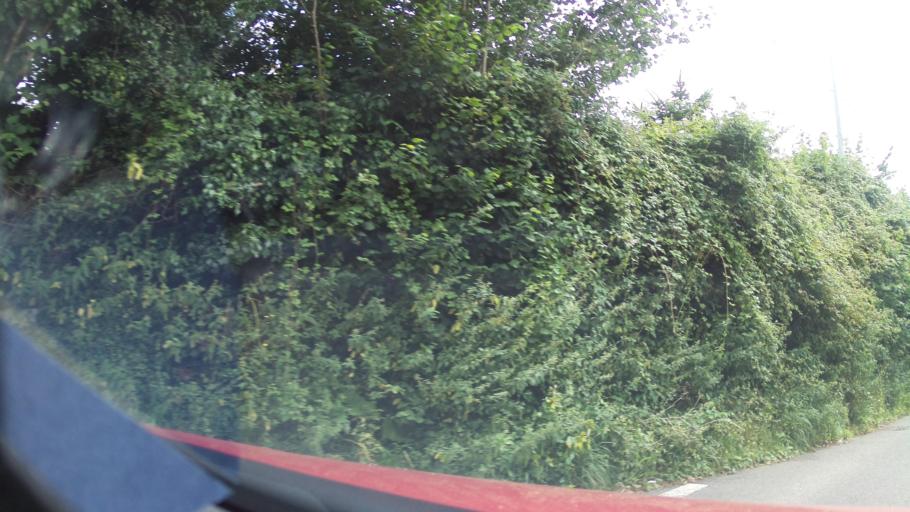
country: GB
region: England
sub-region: Devon
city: Teignmouth
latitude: 50.5632
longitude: -3.5047
